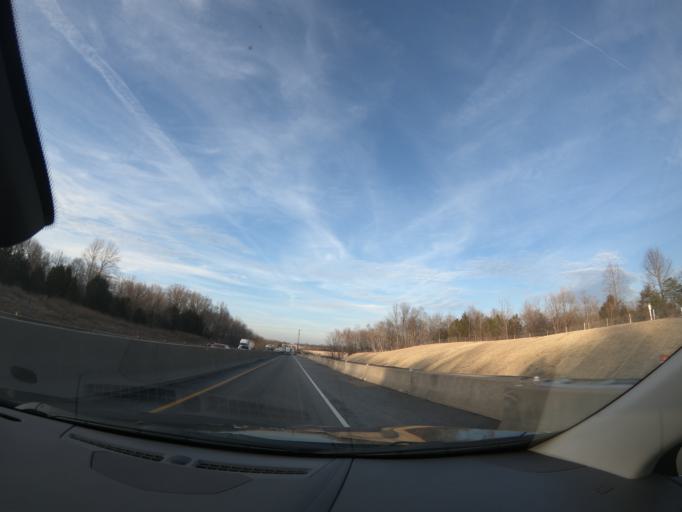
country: US
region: Kentucky
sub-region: Hardin County
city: Elizabethtown
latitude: 37.5583
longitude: -85.8769
